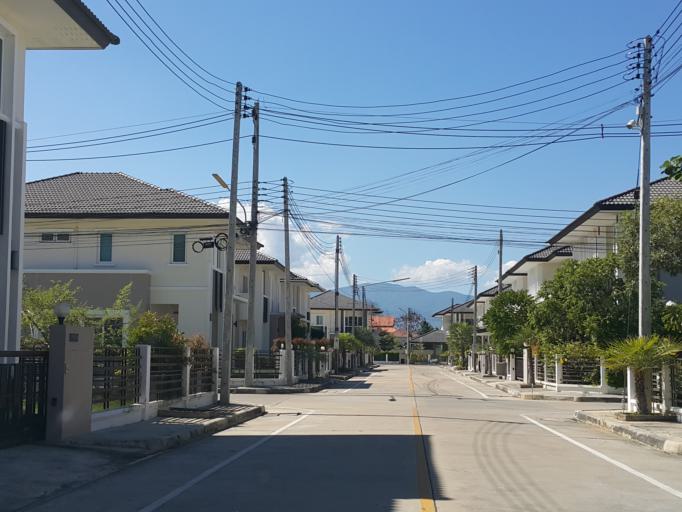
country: TH
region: Chiang Mai
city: San Sai
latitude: 18.8381
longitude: 99.0615
